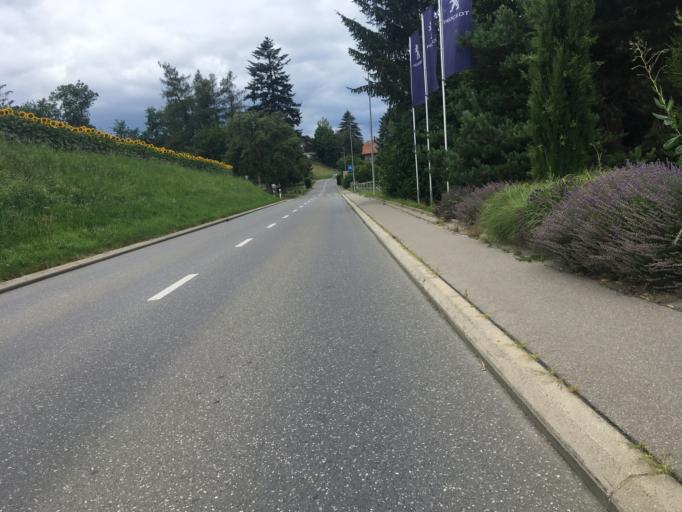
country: CH
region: Vaud
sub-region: Broye-Vully District
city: Payerne
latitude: 46.8714
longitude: 6.9352
